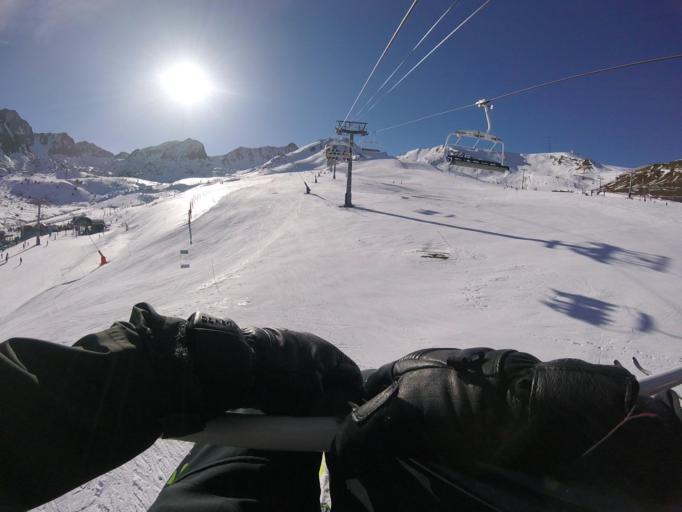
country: AD
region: Encamp
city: Pas de la Casa
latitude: 42.5386
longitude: 1.7324
